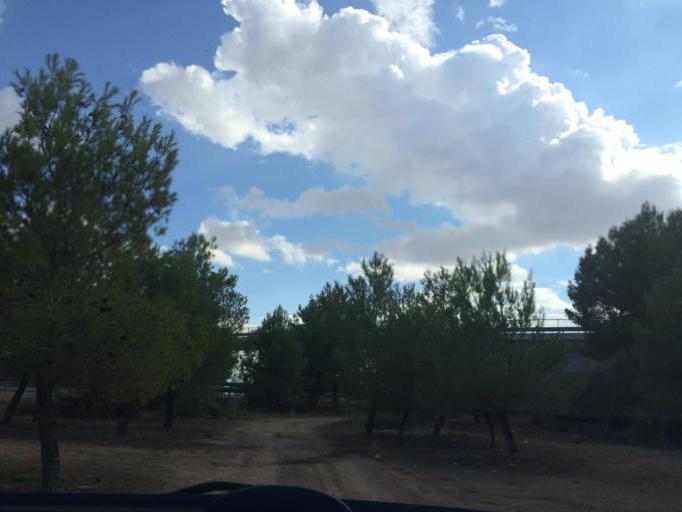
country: ES
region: Castille-La Mancha
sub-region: Provincia de Albacete
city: Albacete
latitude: 38.9481
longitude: -1.8281
